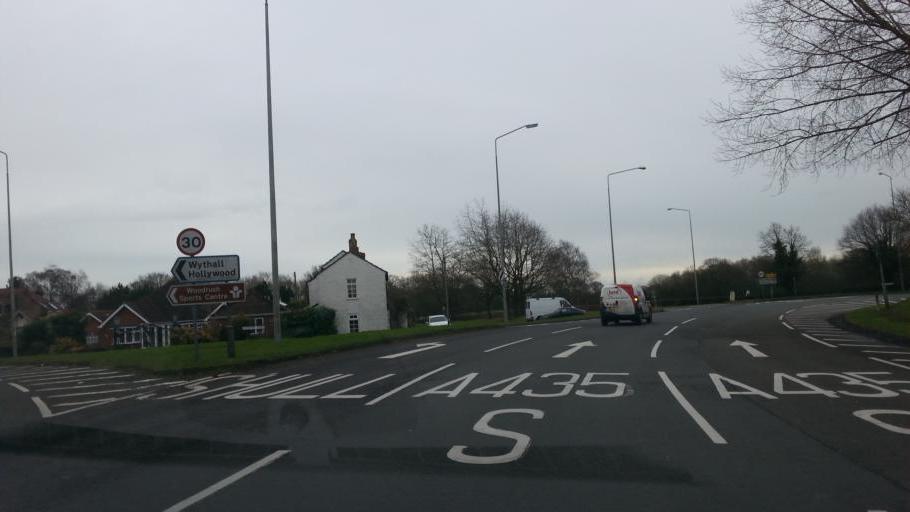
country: GB
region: England
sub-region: Solihull
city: Tidbury Green
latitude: 52.3742
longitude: -1.8860
